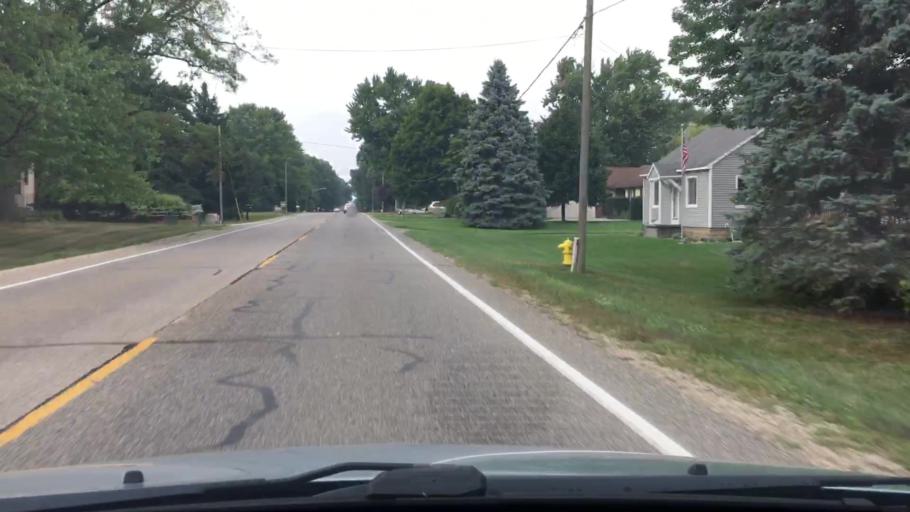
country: US
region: Michigan
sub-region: Ottawa County
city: Hudsonville
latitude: 42.8968
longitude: -85.9018
